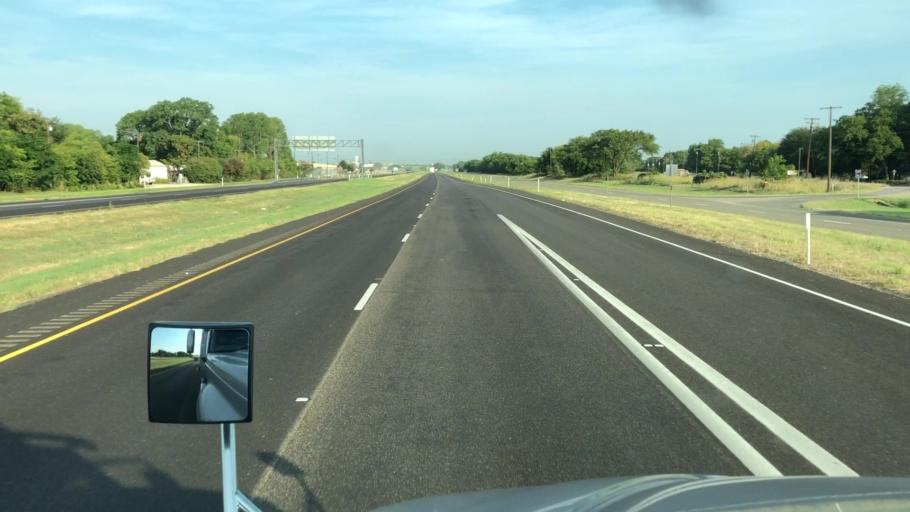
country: US
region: Texas
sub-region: McLennan County
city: Bellmead
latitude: 31.5487
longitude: -97.0742
